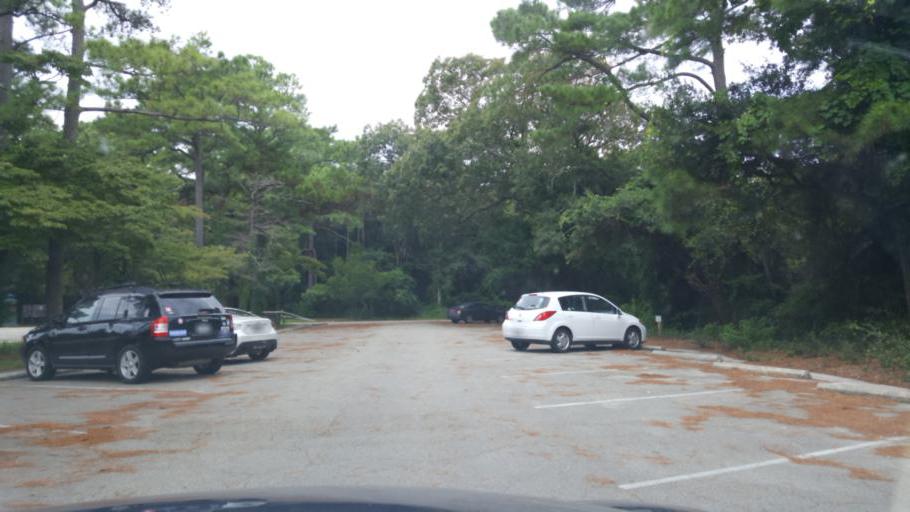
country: US
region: North Carolina
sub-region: Dare County
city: Manteo
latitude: 35.9383
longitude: -75.7070
